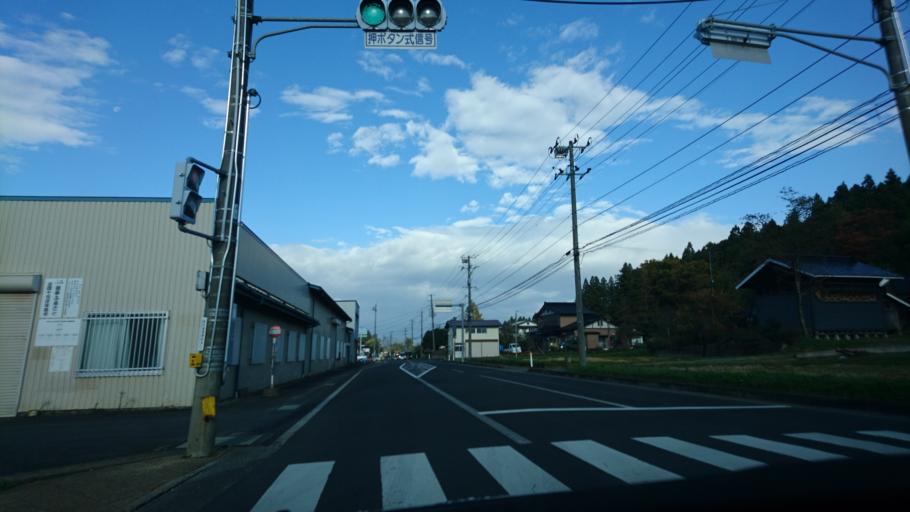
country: JP
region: Iwate
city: Ichinoseki
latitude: 39.0199
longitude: 141.0934
